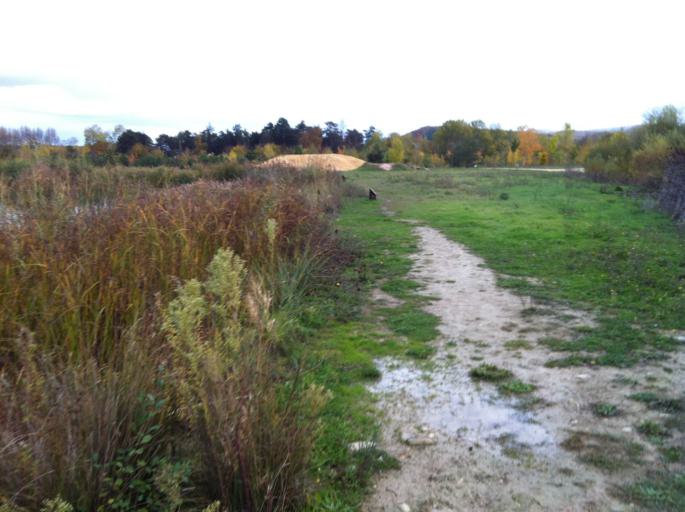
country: ES
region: Basque Country
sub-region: Provincia de Alava
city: Gasteiz / Vitoria
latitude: 42.8302
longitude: -2.6647
